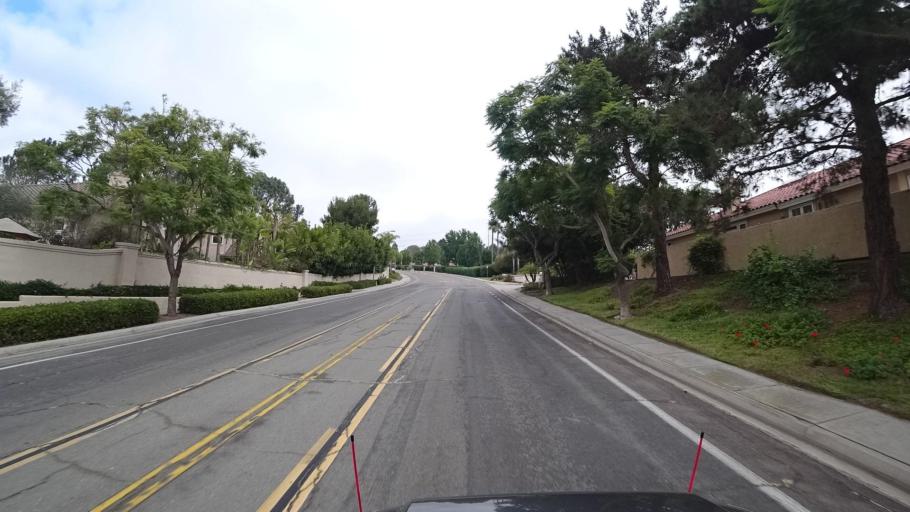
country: US
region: California
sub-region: San Diego County
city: Solana Beach
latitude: 32.9849
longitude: -117.2462
